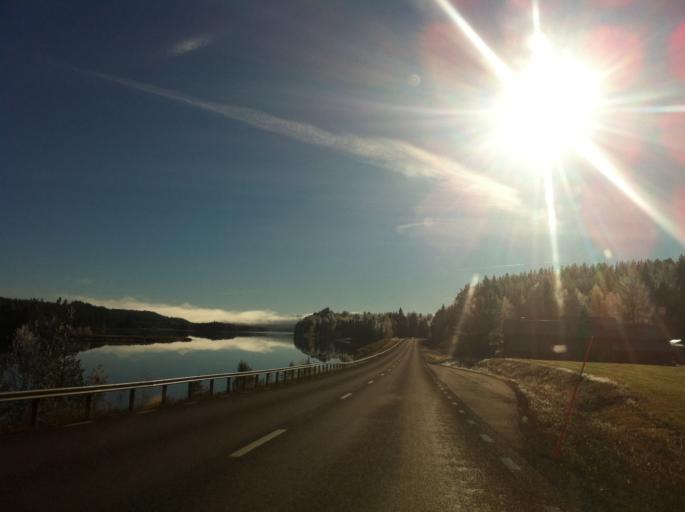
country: NO
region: Hedmark
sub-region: Trysil
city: Innbygda
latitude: 61.7438
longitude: 12.9747
